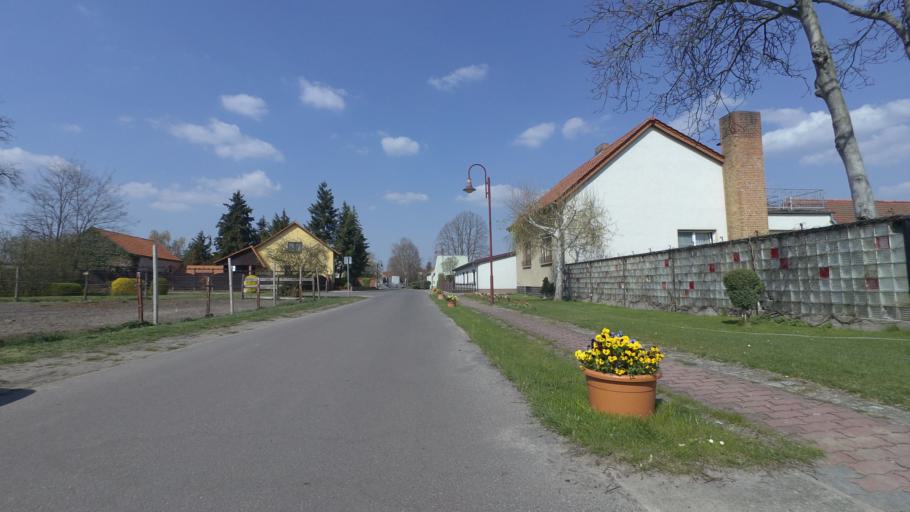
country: DE
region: Brandenburg
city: Mittenwalde
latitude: 52.2206
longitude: 13.5145
